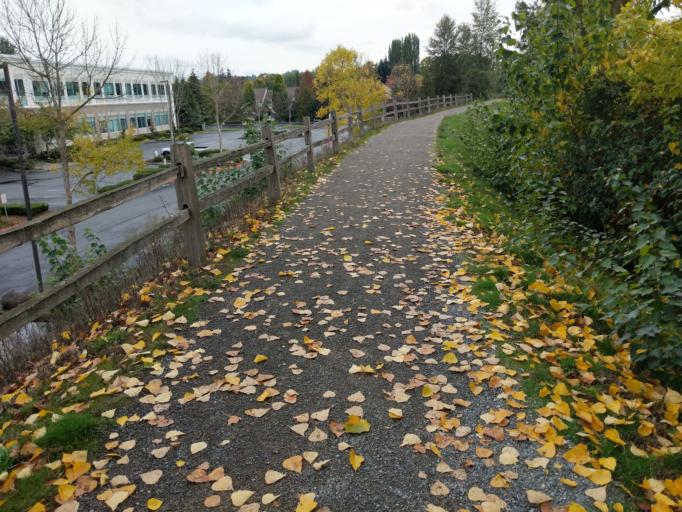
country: US
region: Washington
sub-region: King County
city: Bothell
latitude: 47.7723
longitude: -122.1818
